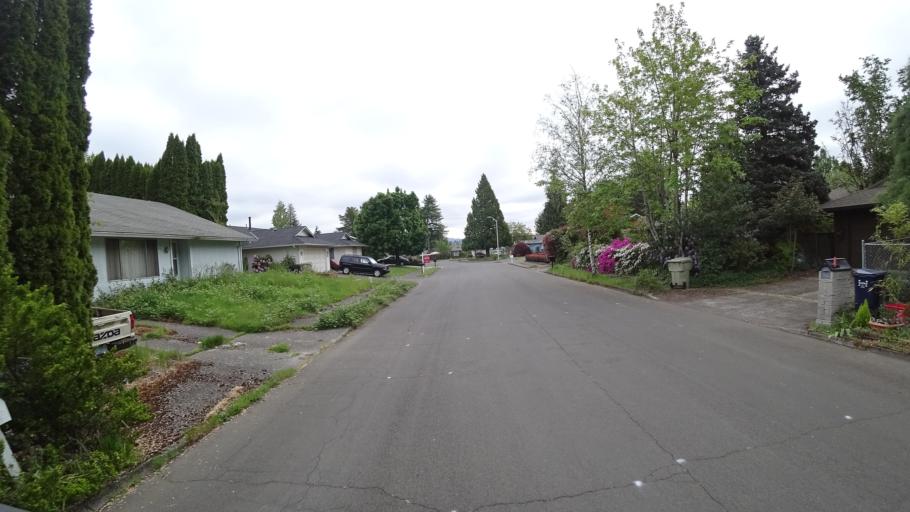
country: US
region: Oregon
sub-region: Washington County
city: Aloha
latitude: 45.5151
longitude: -122.8718
